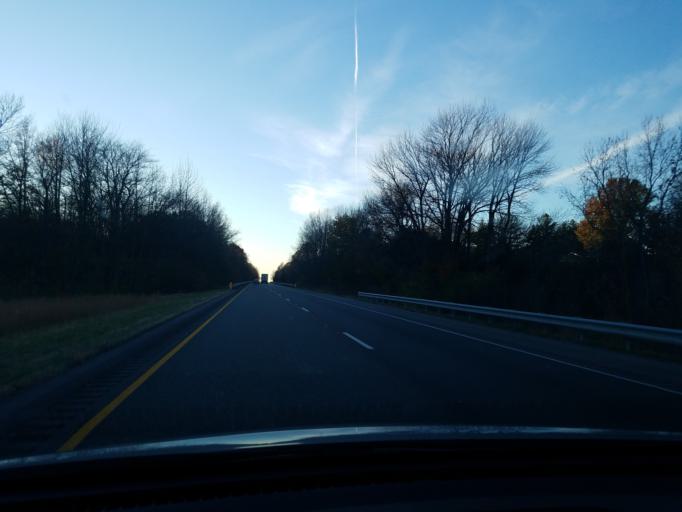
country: US
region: Indiana
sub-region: Gibson County
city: Haubstadt
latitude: 38.1671
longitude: -87.6098
